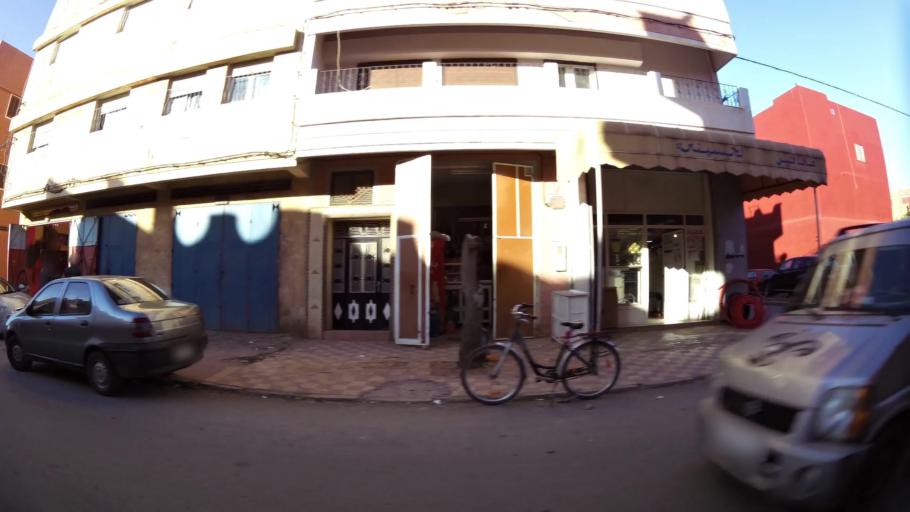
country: MA
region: Oriental
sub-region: Berkane-Taourirt
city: Berkane
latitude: 34.9310
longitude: -2.3232
